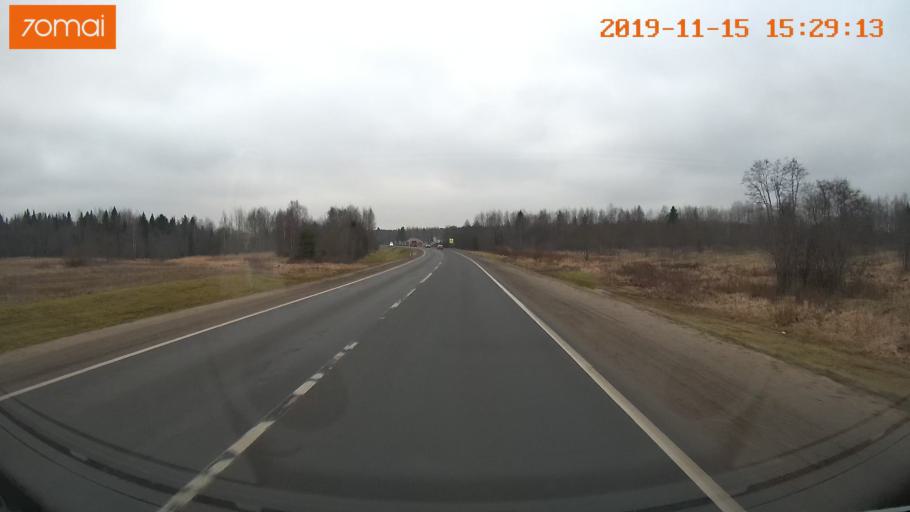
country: RU
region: Jaroslavl
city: Danilov
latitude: 58.1231
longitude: 40.1229
